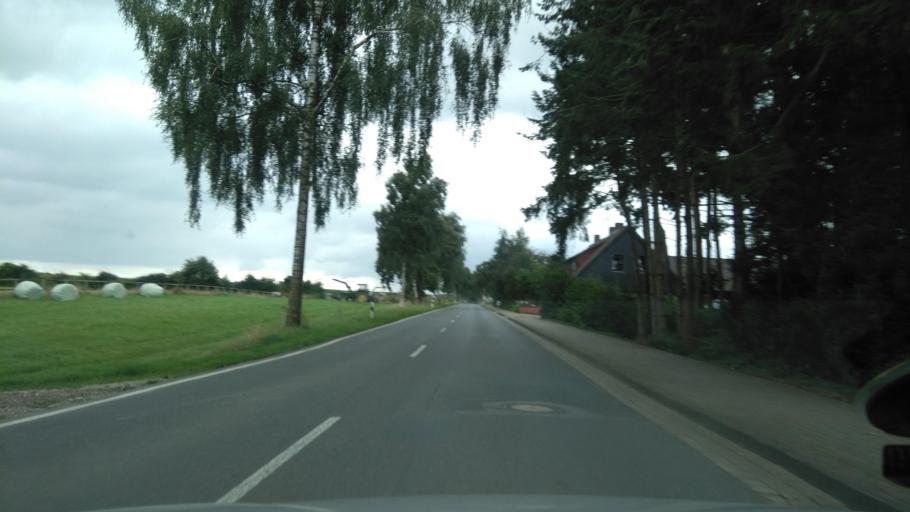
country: DE
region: Lower Saxony
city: Walsrode
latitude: 52.8838
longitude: 9.5756
